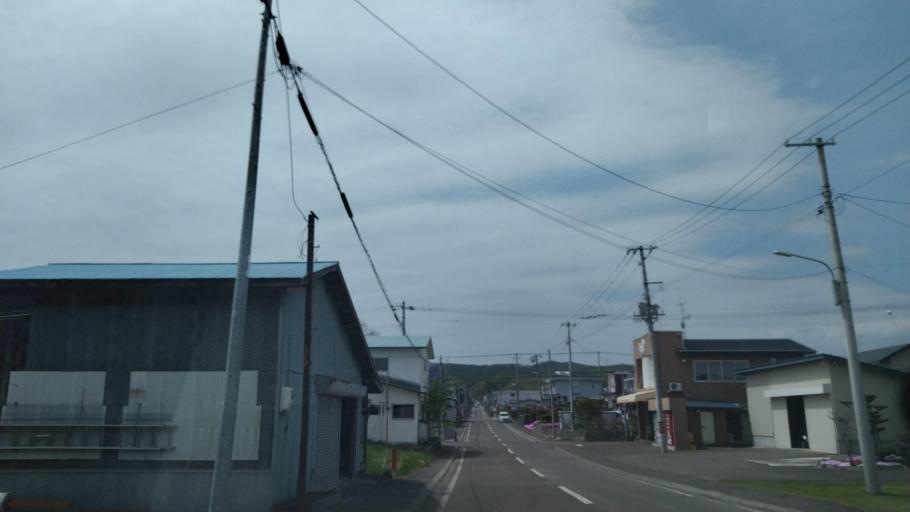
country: JP
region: Hokkaido
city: Otofuke
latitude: 43.2416
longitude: 143.5545
